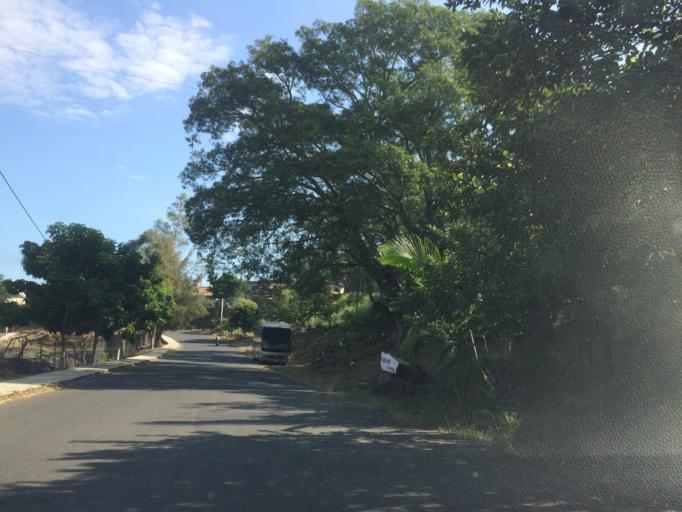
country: MX
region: Nayarit
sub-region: Ahuacatlan
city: Ahuacatlan
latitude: 21.0497
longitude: -104.4758
